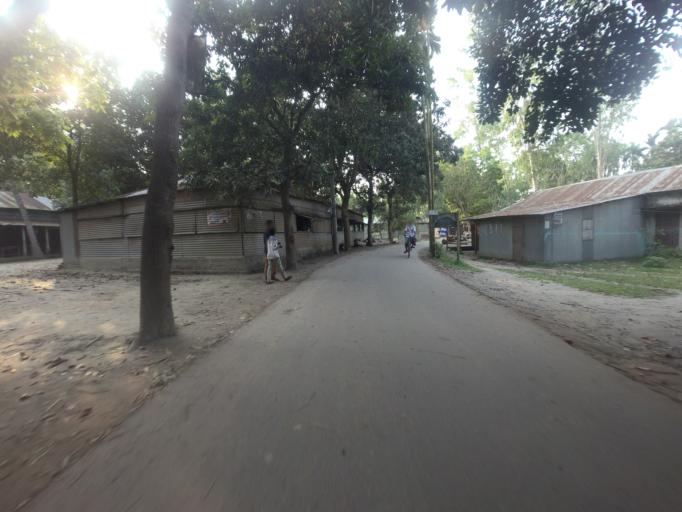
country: BD
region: Rajshahi
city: Sirajganj
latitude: 24.3202
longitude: 89.6940
